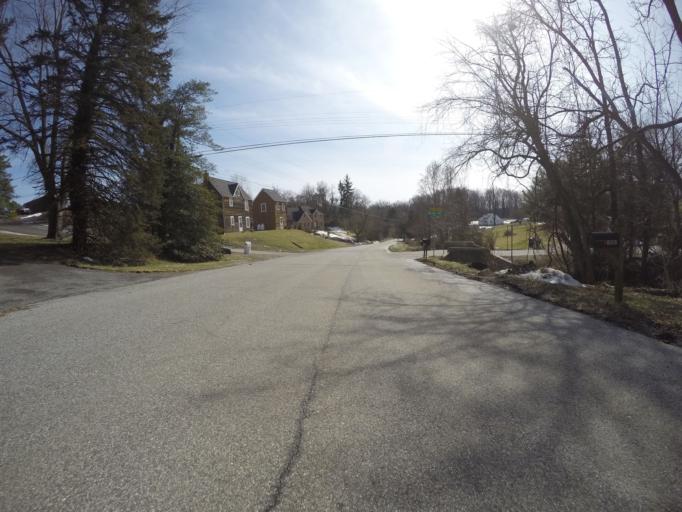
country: US
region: Maryland
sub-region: Baltimore County
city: Hunt Valley
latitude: 39.5207
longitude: -76.6574
